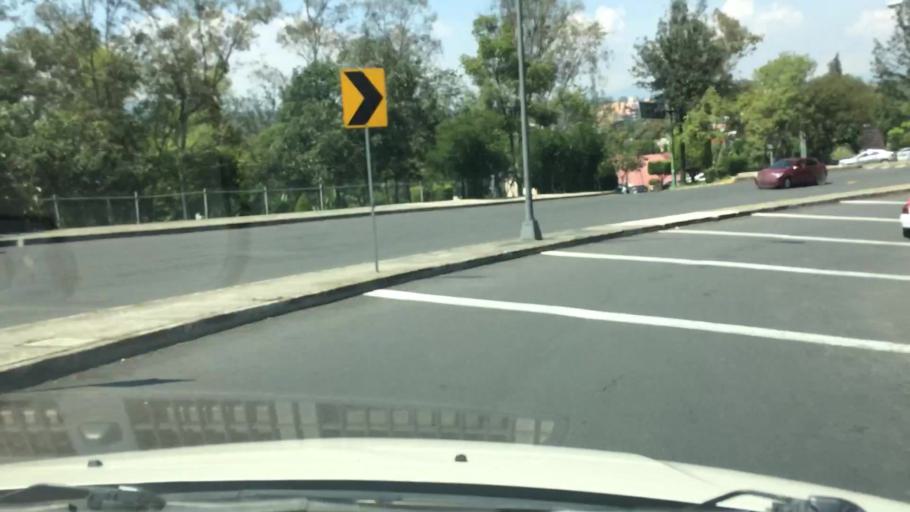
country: MX
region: Mexico City
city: Tlalpan
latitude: 19.3012
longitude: -99.1921
